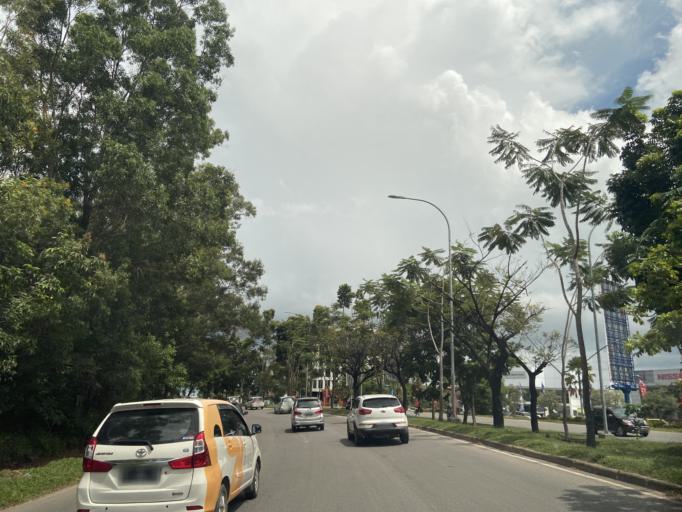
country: SG
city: Singapore
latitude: 1.1302
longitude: 104.0171
